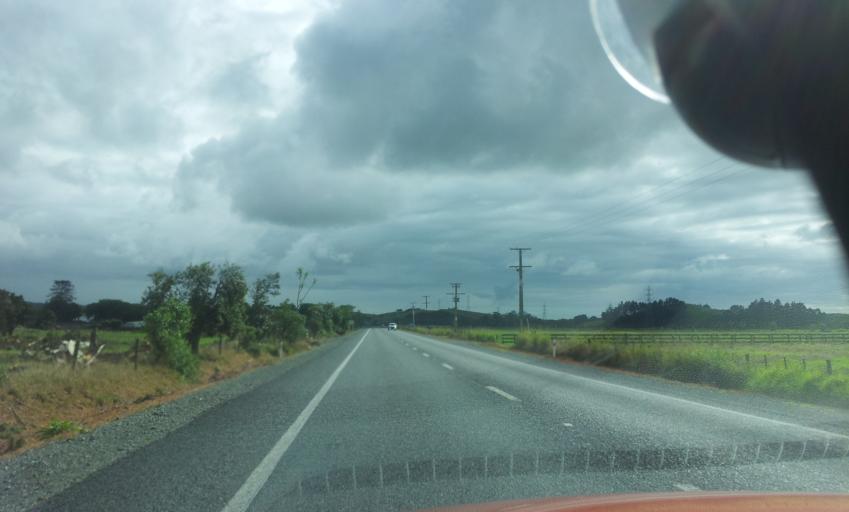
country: NZ
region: Northland
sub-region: Whangarei
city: Ruakaka
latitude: -36.0250
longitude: 174.4175
